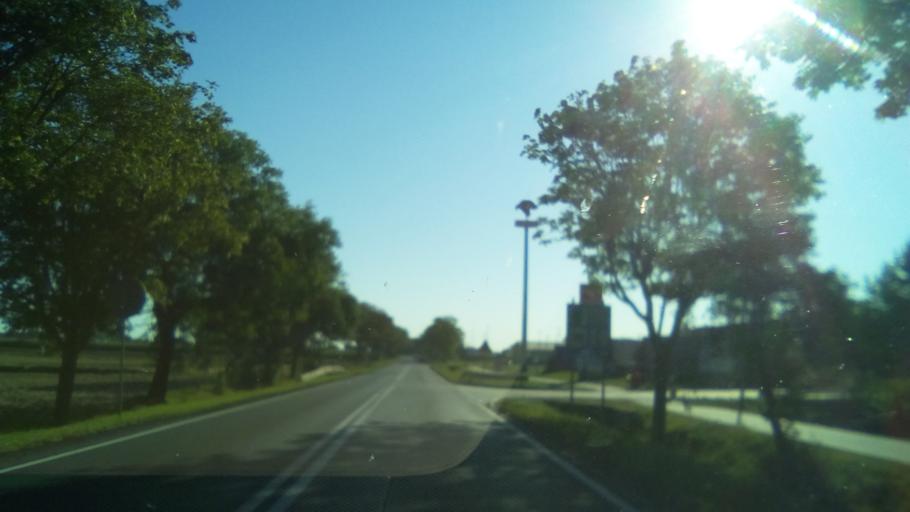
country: PL
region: Kujawsko-Pomorskie
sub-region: Powiat radziejowski
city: Radziejow
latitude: 52.6306
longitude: 18.5269
